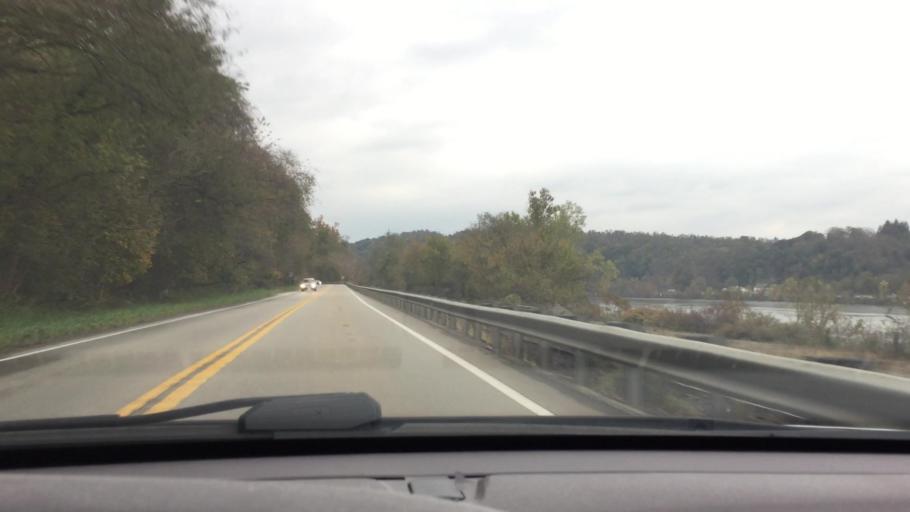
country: US
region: Pennsylvania
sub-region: Fayette County
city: Fairhope
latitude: 40.1037
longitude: -79.8466
